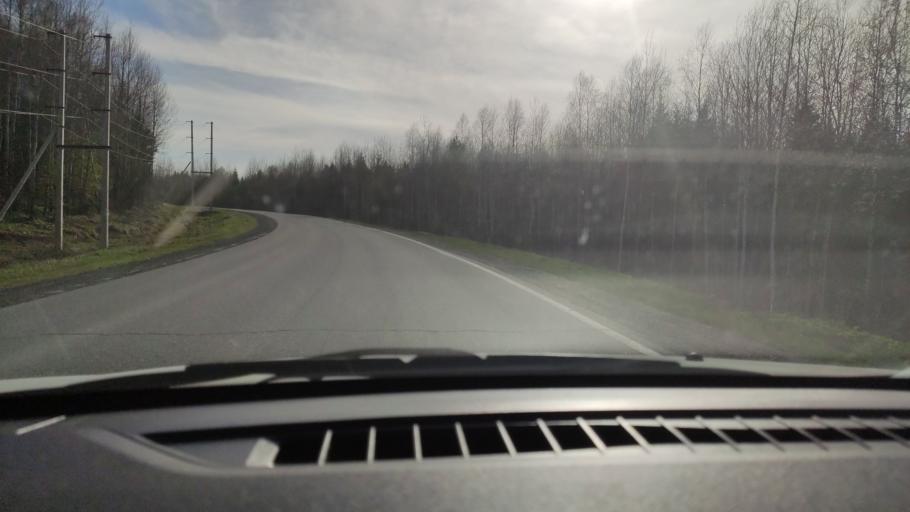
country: RU
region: Perm
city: Novyye Lyady
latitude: 57.9598
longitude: 56.5389
